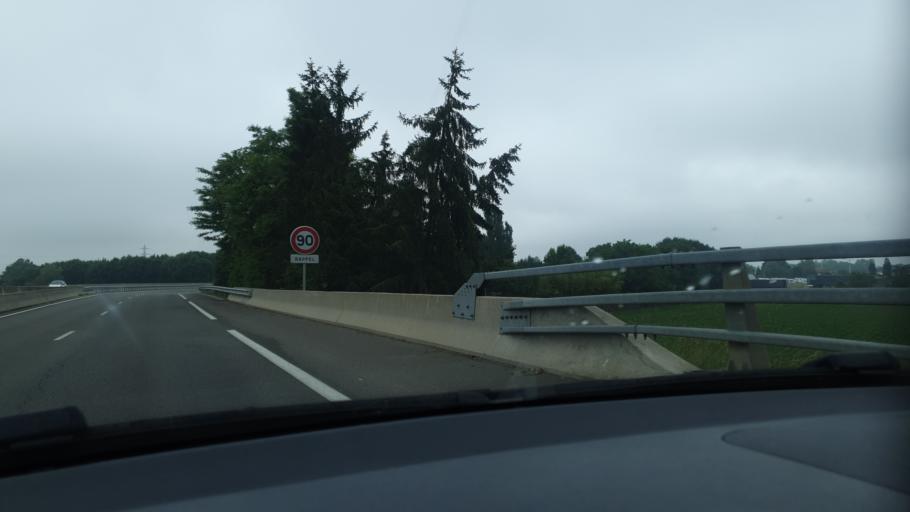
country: FR
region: Midi-Pyrenees
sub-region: Departement des Hautes-Pyrenees
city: Juillan
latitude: 43.2298
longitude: 0.0440
